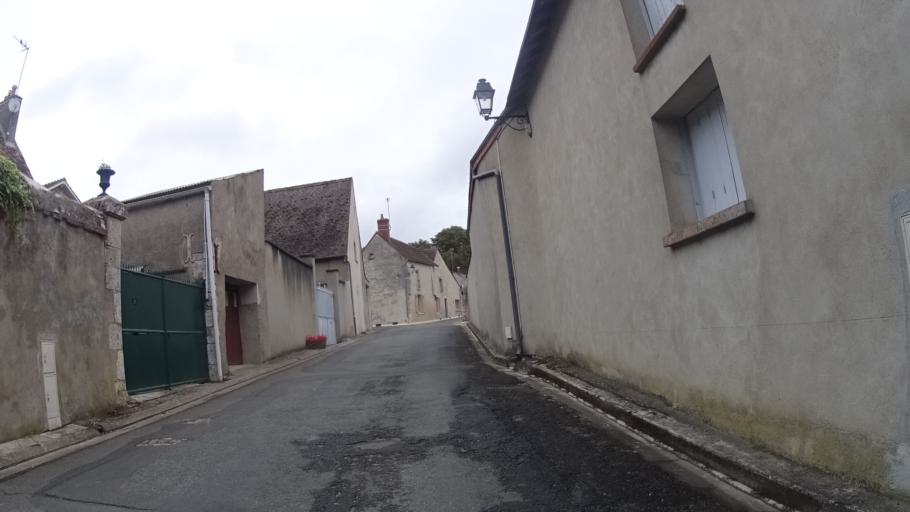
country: FR
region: Centre
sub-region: Departement du Loir-et-Cher
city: Montlivault
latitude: 47.6560
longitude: 1.4337
